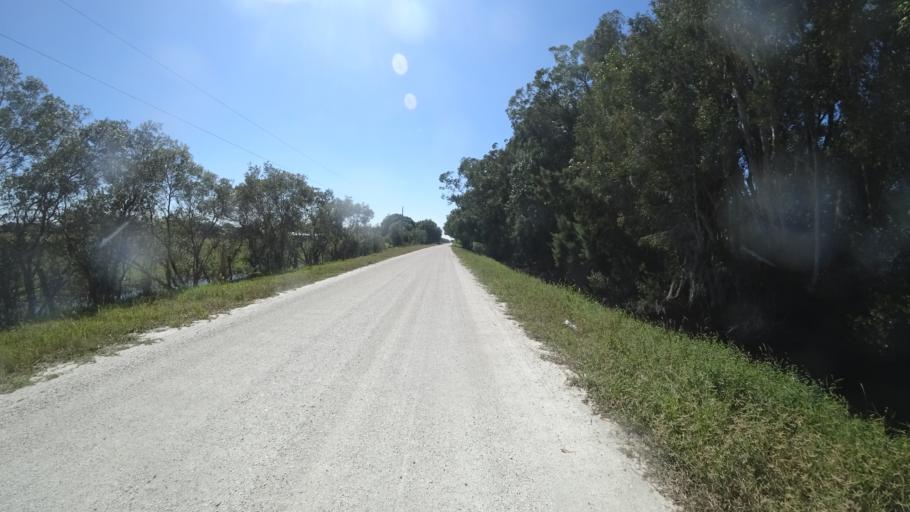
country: US
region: Florida
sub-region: DeSoto County
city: Arcadia
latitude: 27.3259
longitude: -82.0804
